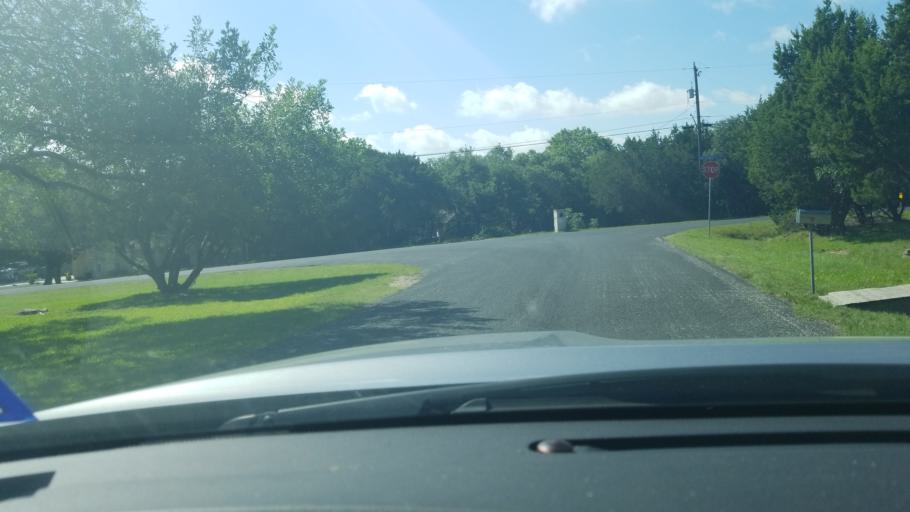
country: US
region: Texas
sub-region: Bexar County
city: Timberwood Park
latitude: 29.7037
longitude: -98.4865
